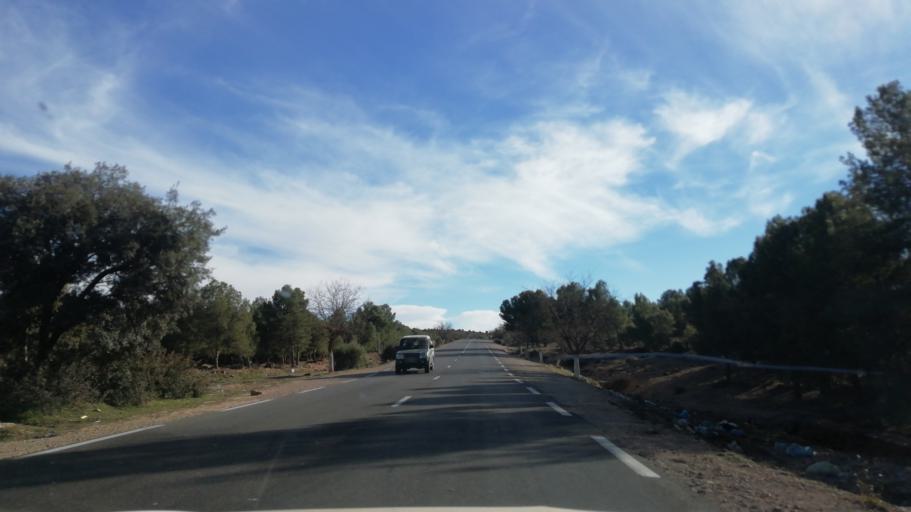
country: DZ
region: Tlemcen
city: Sebdou
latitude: 34.5902
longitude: -1.3183
